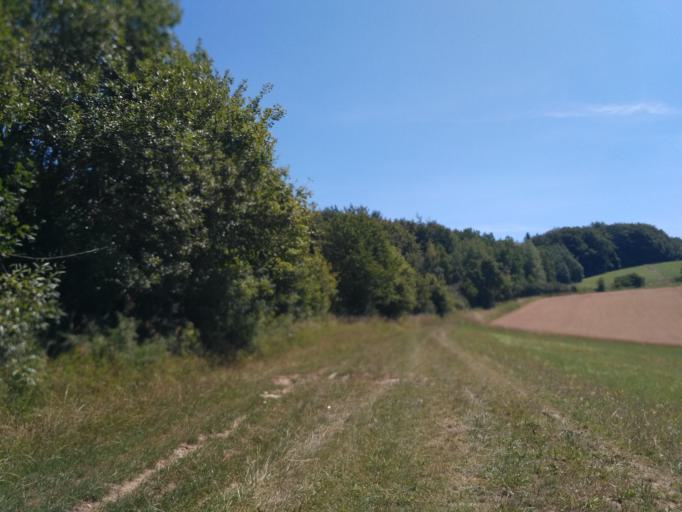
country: PL
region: Subcarpathian Voivodeship
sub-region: Powiat sanocki
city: Bukowsko
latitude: 49.5138
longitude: 22.0525
